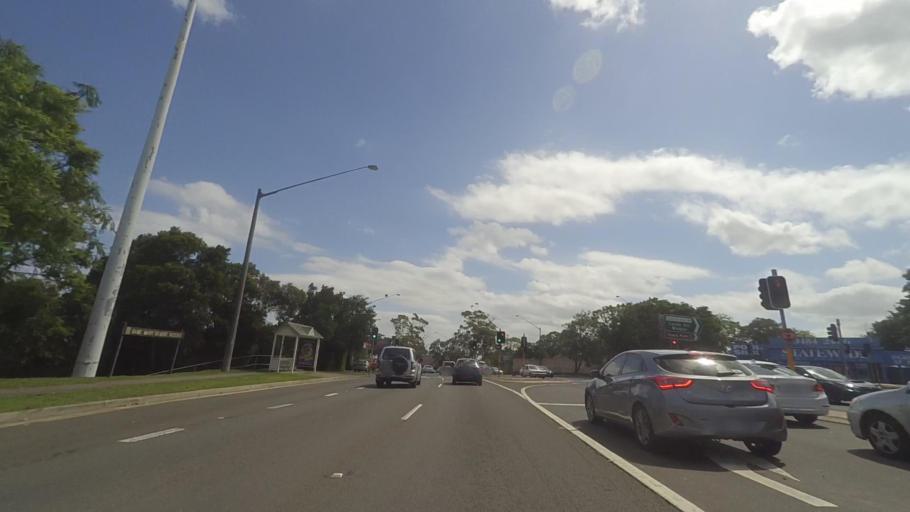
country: AU
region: New South Wales
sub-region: The Hills Shire
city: West Pennant
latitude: -33.7480
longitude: 151.0501
